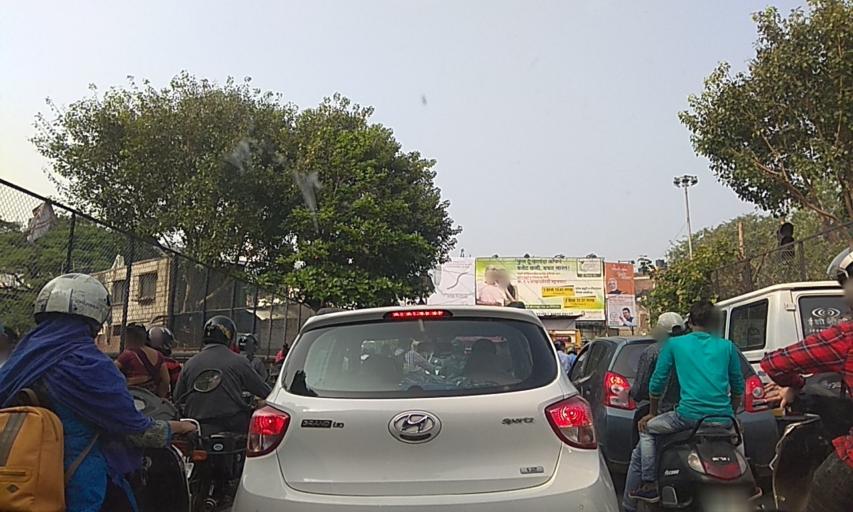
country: IN
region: Maharashtra
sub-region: Pune Division
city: Pune
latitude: 18.5047
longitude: 73.8392
